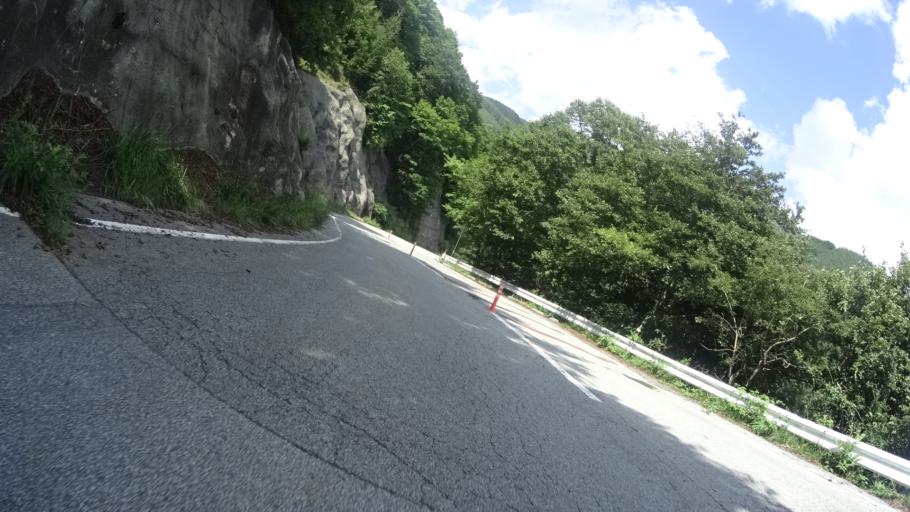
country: JP
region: Yamanashi
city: Enzan
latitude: 35.8009
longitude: 138.6691
